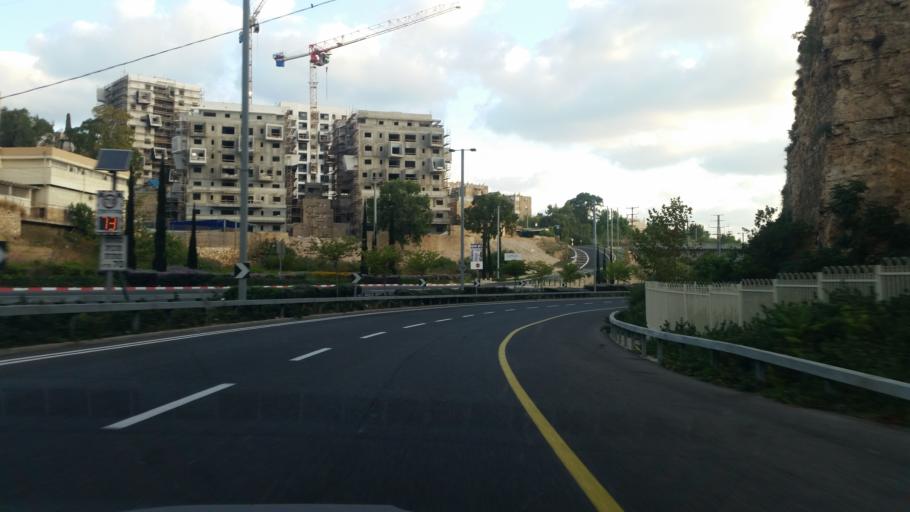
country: IL
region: Haifa
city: Haifa
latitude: 32.8014
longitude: 35.0050
